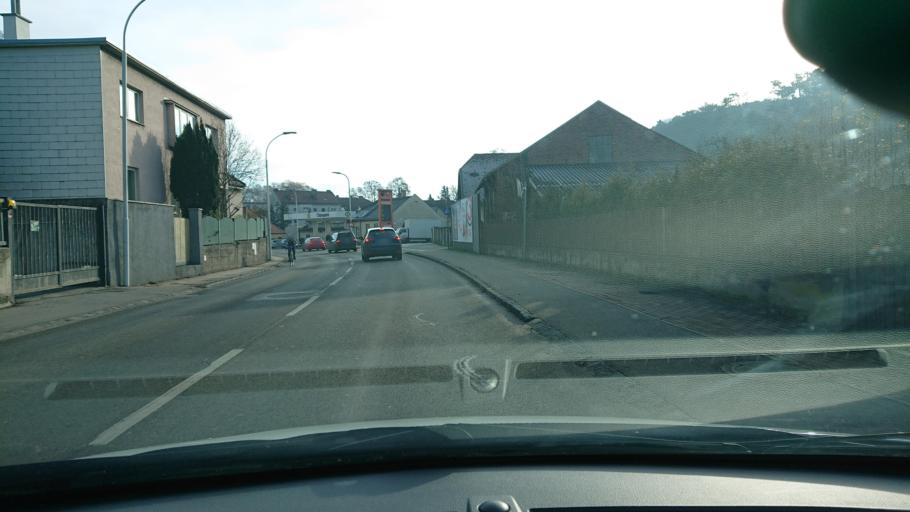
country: AT
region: Lower Austria
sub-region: Politischer Bezirk Baden
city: Hirtenberg
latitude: 47.9311
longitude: 16.1737
